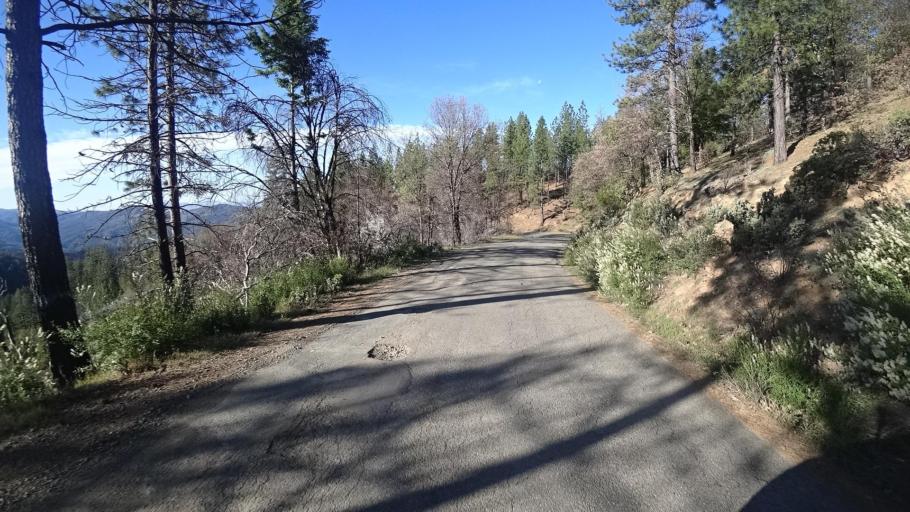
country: US
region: California
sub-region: Lake County
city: Upper Lake
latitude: 39.2857
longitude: -122.9267
